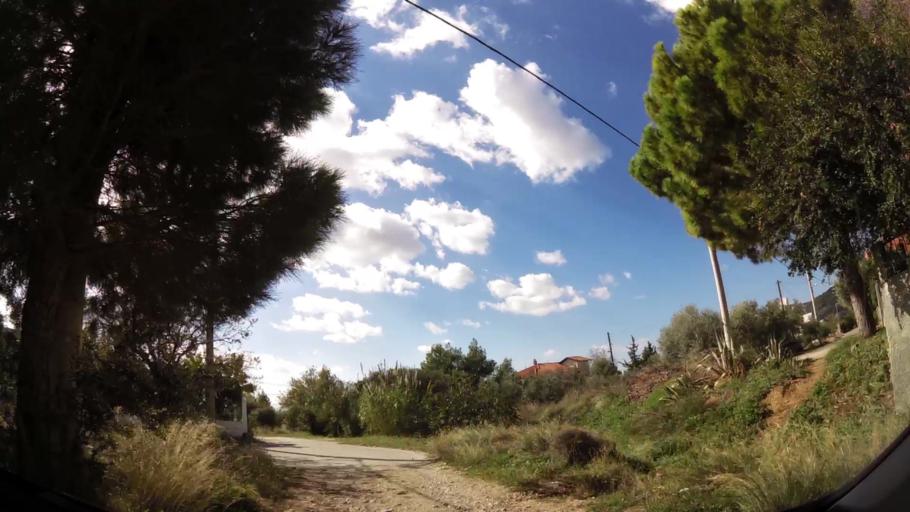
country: GR
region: Attica
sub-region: Nomarchia Anatolikis Attikis
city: Thrakomakedones
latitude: 38.1175
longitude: 23.7480
